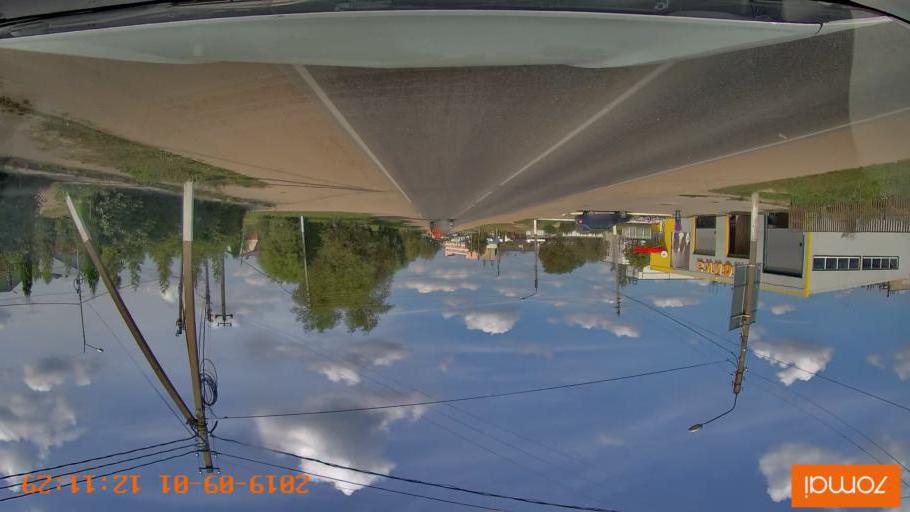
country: RU
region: Kaluga
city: Maloyaroslavets
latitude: 54.9994
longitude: 36.4392
